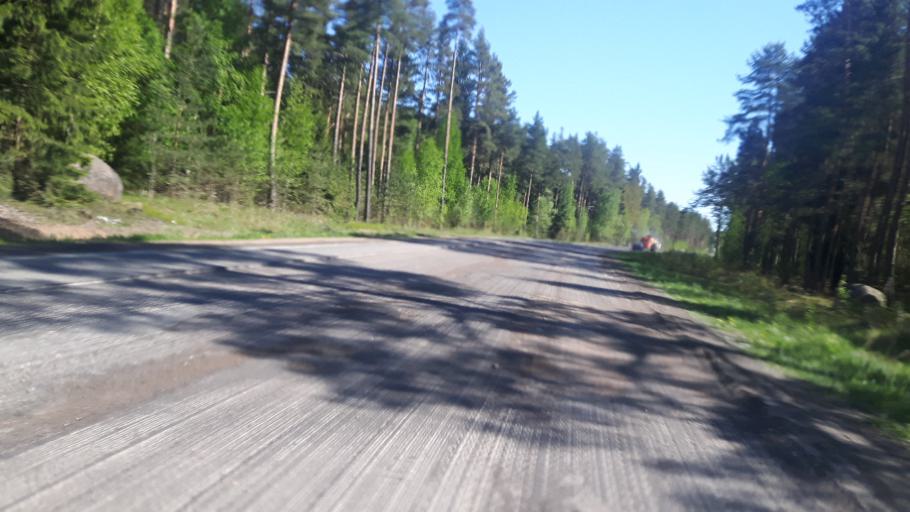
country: RU
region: Leningrad
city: Sosnovyy Bor
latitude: 60.2273
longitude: 29.0042
